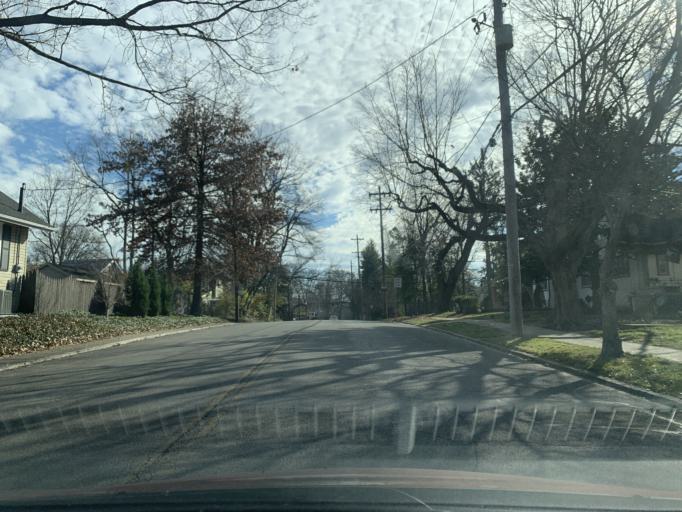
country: US
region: Kentucky
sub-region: Jefferson County
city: Saint Matthews
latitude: 38.2499
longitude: -85.6817
